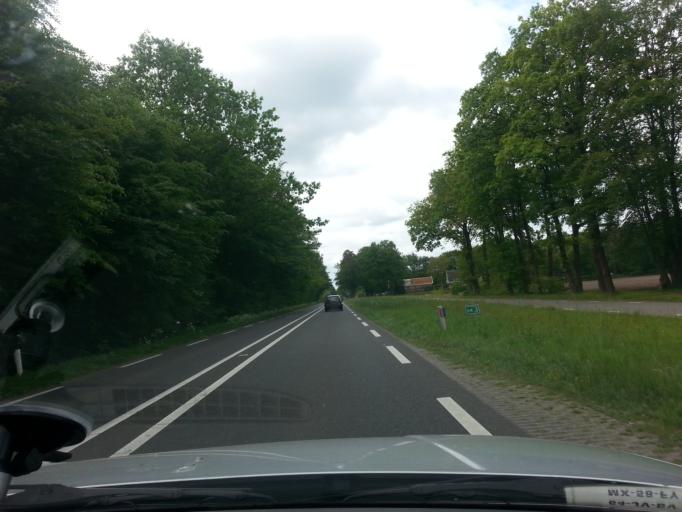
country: NL
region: Overijssel
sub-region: Gemeente Oldenzaal
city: Oldenzaal
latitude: 52.3479
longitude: 6.9722
